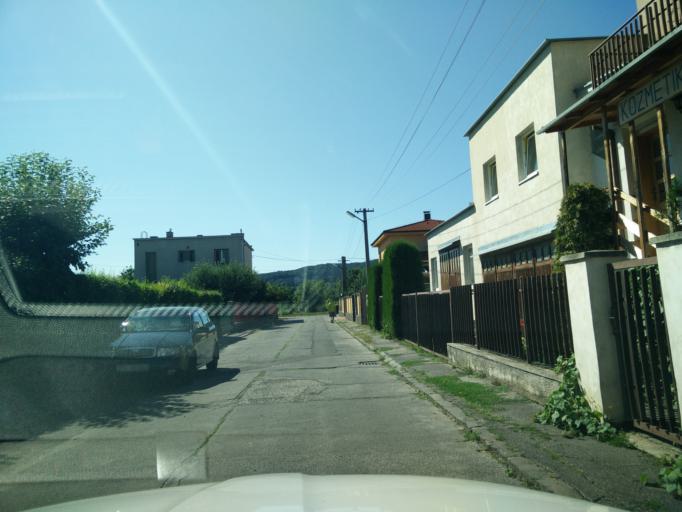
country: SK
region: Nitriansky
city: Bojnice
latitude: 48.7709
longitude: 18.5970
